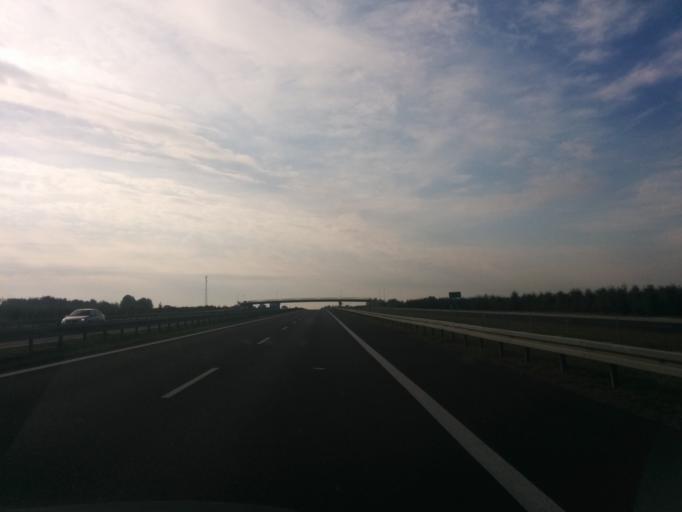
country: PL
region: Masovian Voivodeship
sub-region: Powiat grojecki
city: Jasieniec
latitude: 51.7845
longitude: 20.8945
